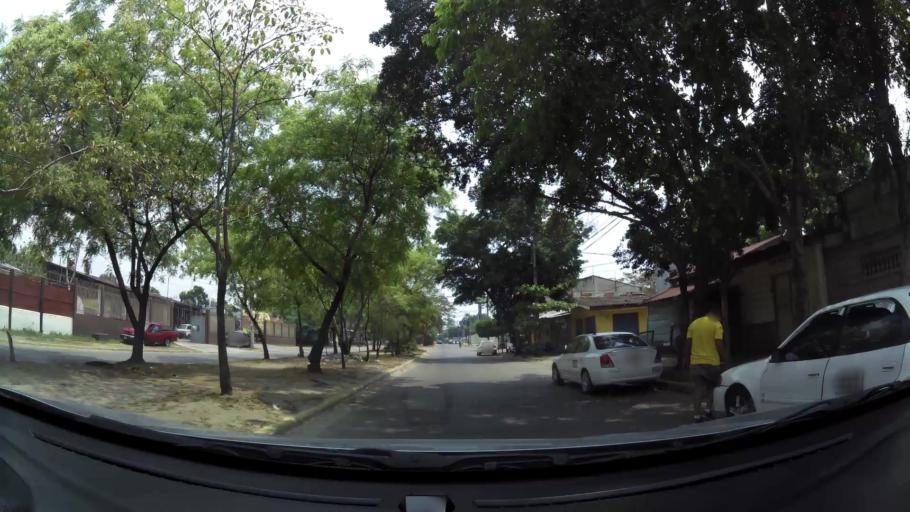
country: HN
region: Cortes
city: San Pedro Sula
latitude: 15.4881
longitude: -88.0197
